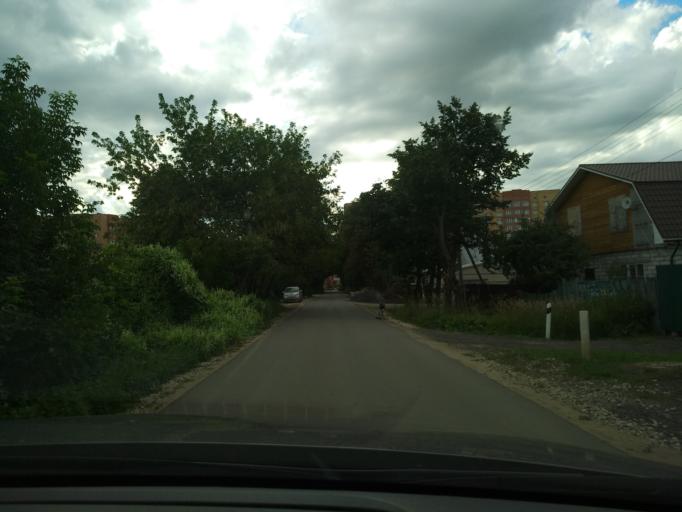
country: RU
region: Moskovskaya
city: Yegor'yevsk
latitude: 55.3676
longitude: 39.0830
